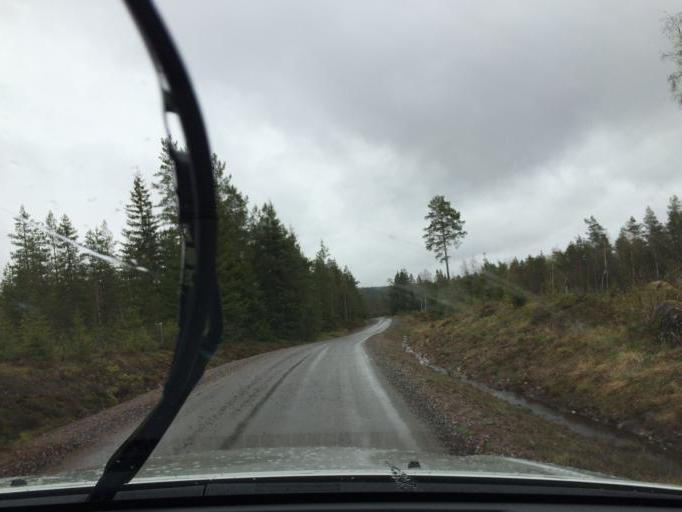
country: SE
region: Dalarna
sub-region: Ludvika Kommun
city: Abborrberget
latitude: 60.0383
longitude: 14.6500
